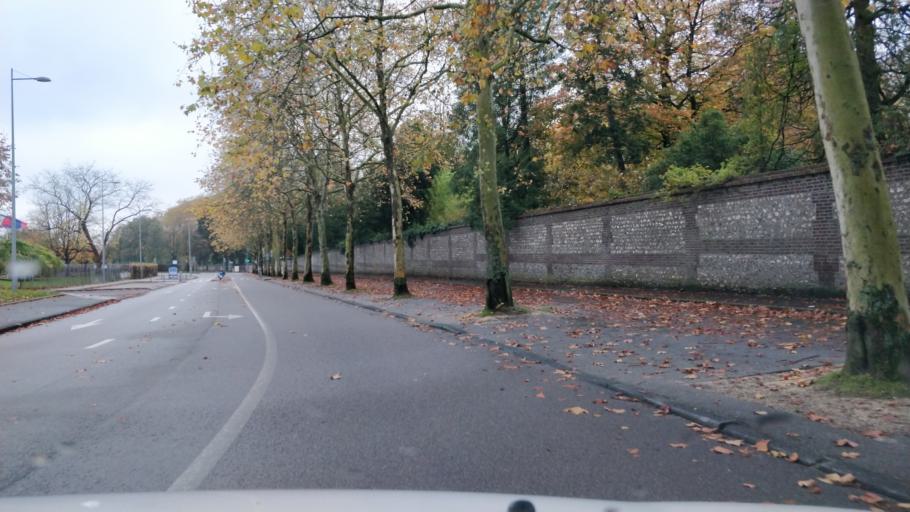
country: FR
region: Haute-Normandie
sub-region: Departement de la Seine-Maritime
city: Bihorel
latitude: 49.4516
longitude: 1.1197
